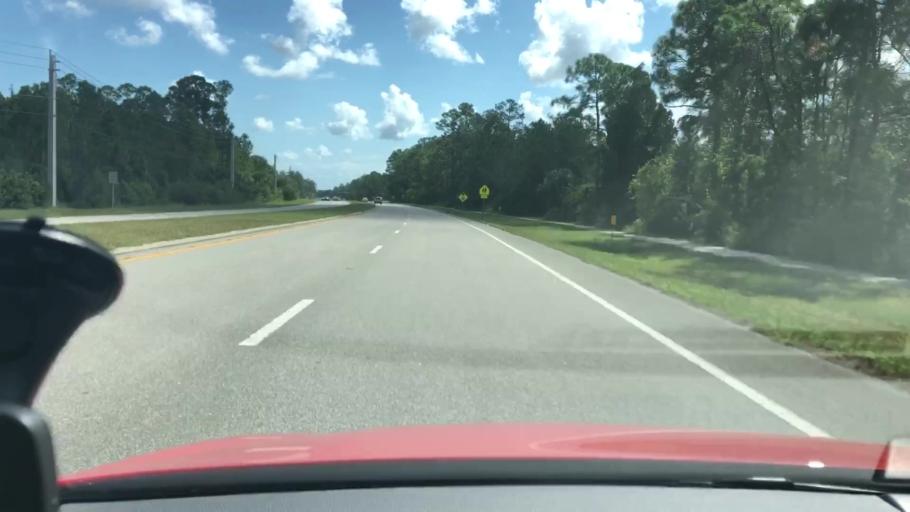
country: US
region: Florida
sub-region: Volusia County
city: Holly Hill
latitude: 29.2436
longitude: -81.0934
